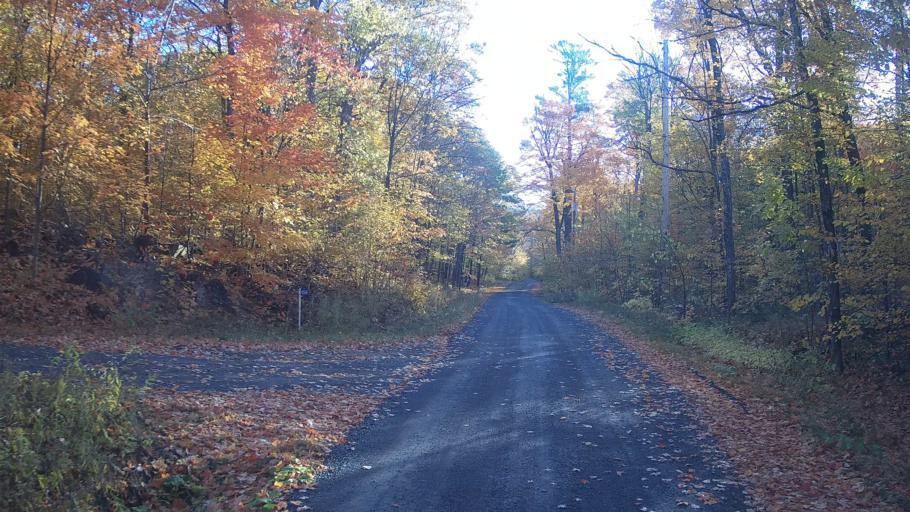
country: CA
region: Ontario
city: Arnprior
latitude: 45.3449
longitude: -76.3400
